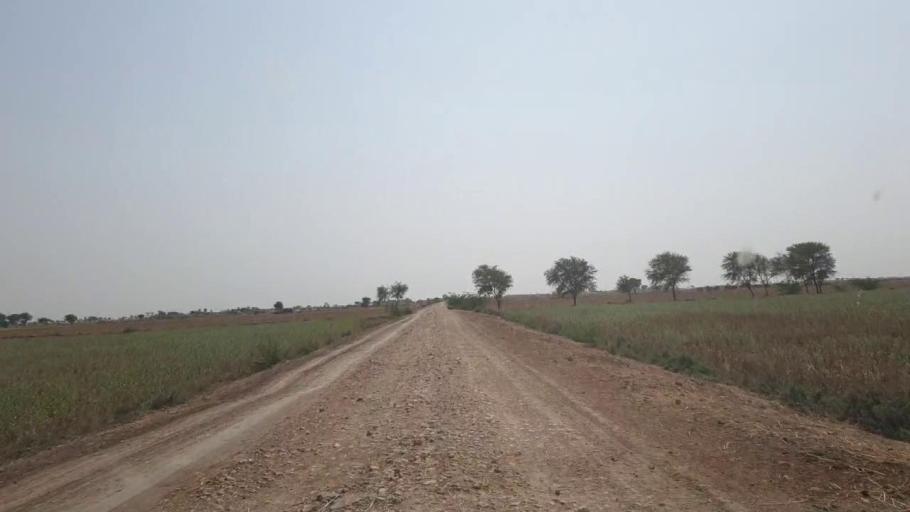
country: PK
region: Sindh
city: Jati
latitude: 24.4348
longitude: 68.5523
